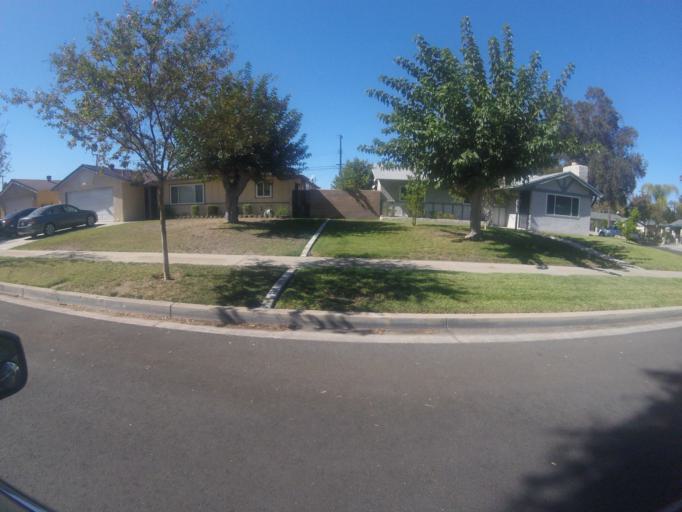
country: US
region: California
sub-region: San Bernardino County
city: Redlands
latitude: 34.0783
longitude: -117.1781
